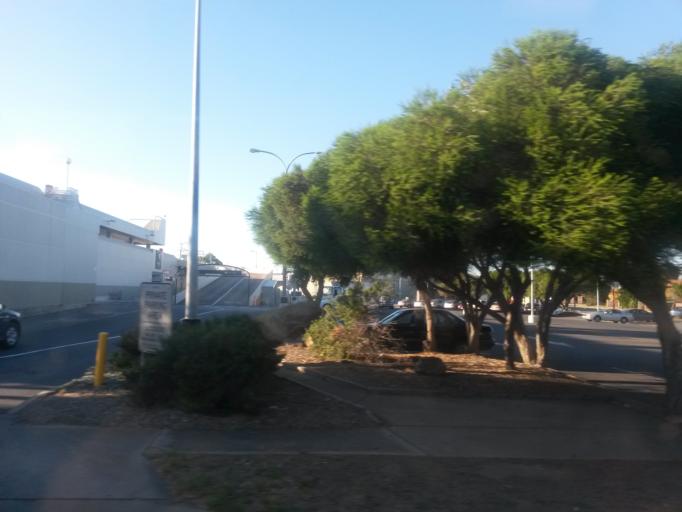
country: AU
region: South Australia
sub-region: Charles Sturt
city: Woodville North
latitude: -34.8723
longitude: 138.5490
